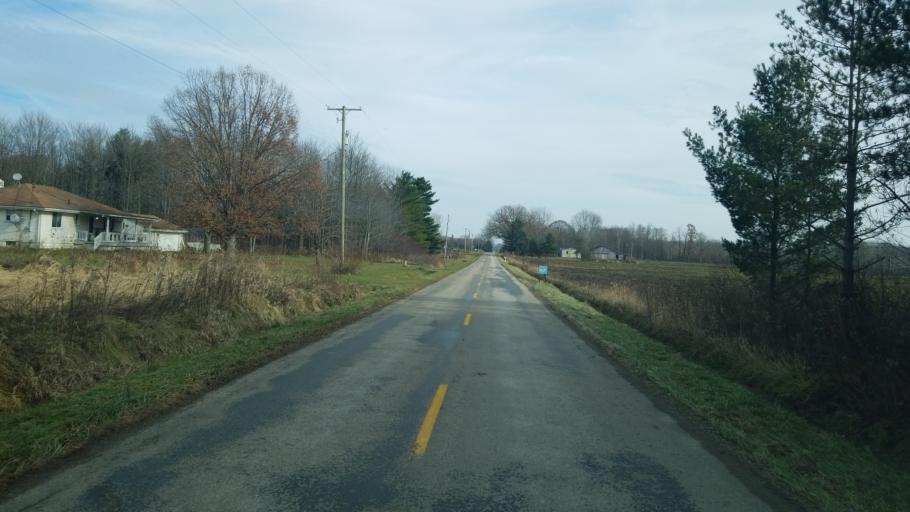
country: US
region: Ohio
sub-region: Ashtabula County
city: Andover
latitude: 41.6353
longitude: -80.6937
